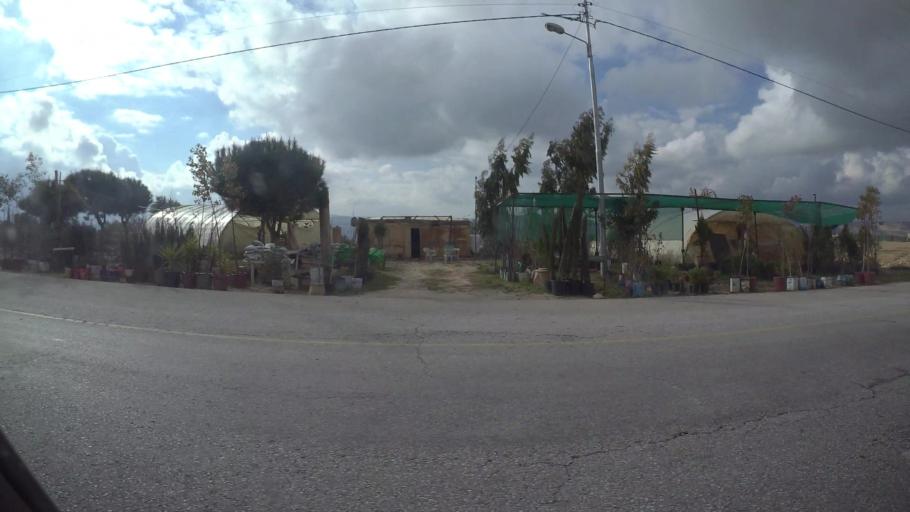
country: JO
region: Amman
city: Al Jubayhah
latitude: 32.0738
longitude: 35.8782
